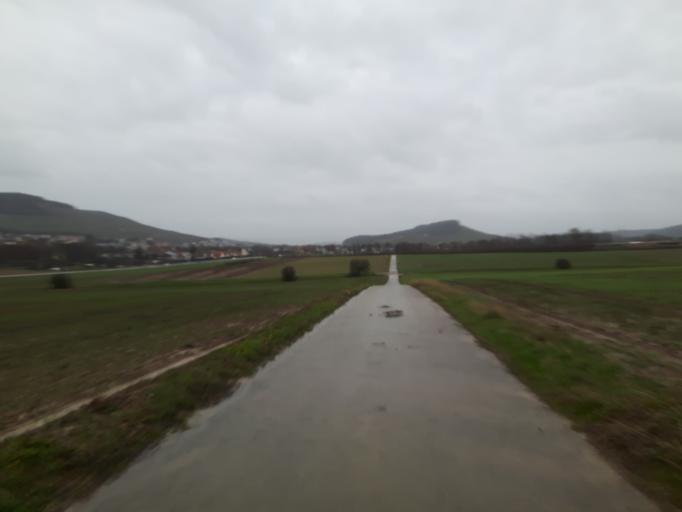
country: DE
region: Baden-Wuerttemberg
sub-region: Regierungsbezirk Stuttgart
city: Erlenbach
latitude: 49.1739
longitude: 9.2494
